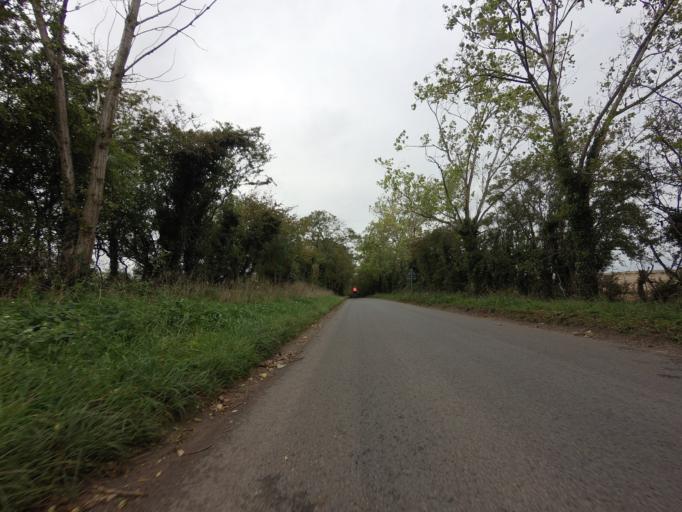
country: GB
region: England
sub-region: Cambridgeshire
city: Duxford
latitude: 52.0448
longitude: 0.1651
